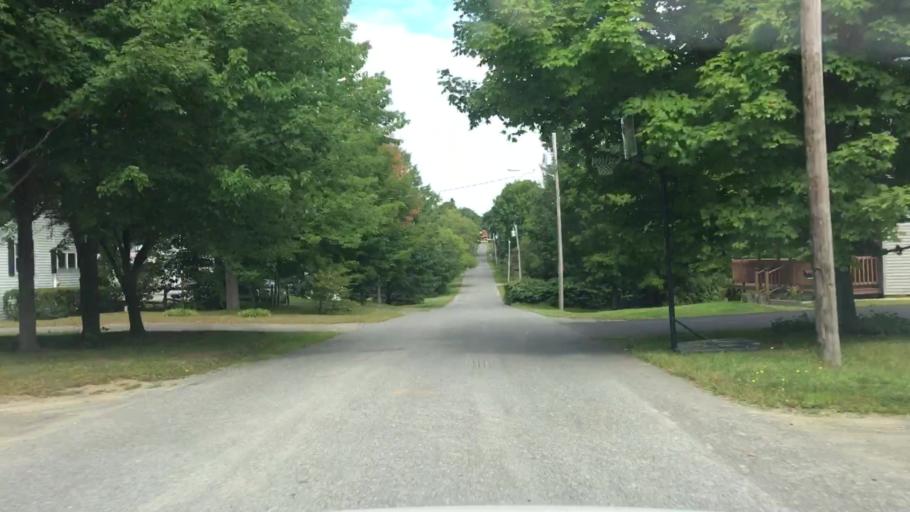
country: US
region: Maine
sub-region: Piscataquis County
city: Dover-Foxcroft
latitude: 45.1873
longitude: -69.2221
